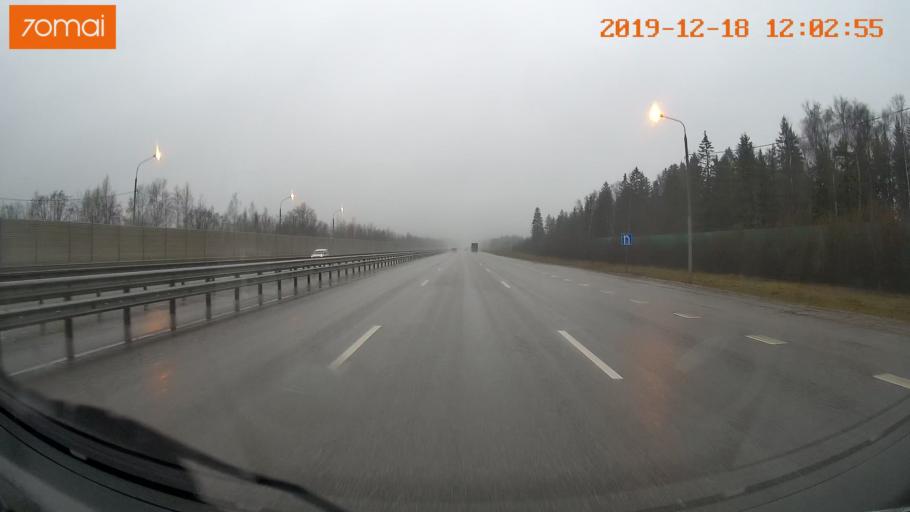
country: RU
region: Moskovskaya
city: Kostrovo
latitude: 55.8576
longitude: 36.7584
